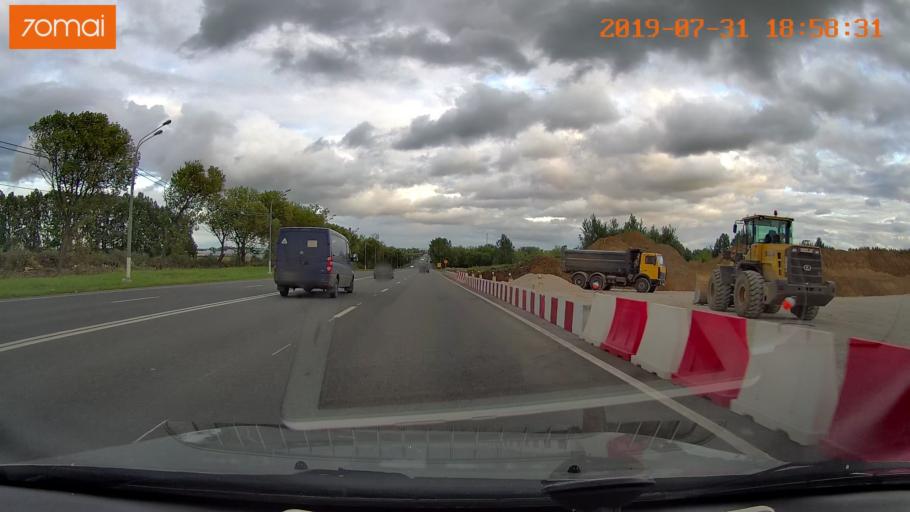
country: RU
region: Moskovskaya
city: Raduzhnyy
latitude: 55.1463
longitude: 38.7053
